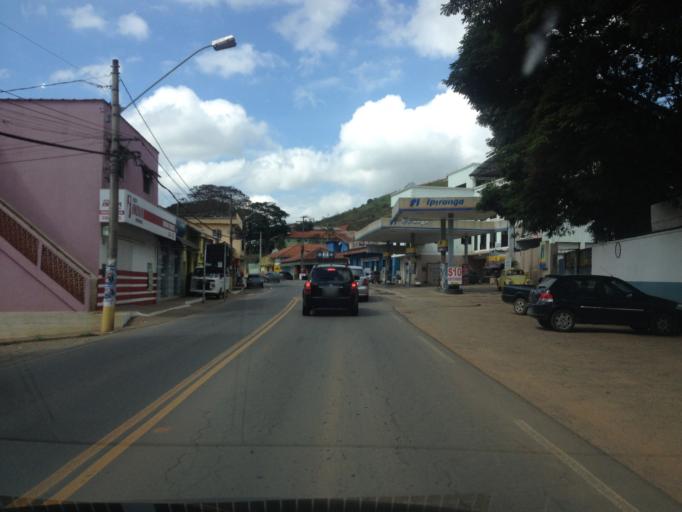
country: BR
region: Minas Gerais
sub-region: Itanhandu
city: Itanhandu
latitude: -22.1970
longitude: -44.9738
